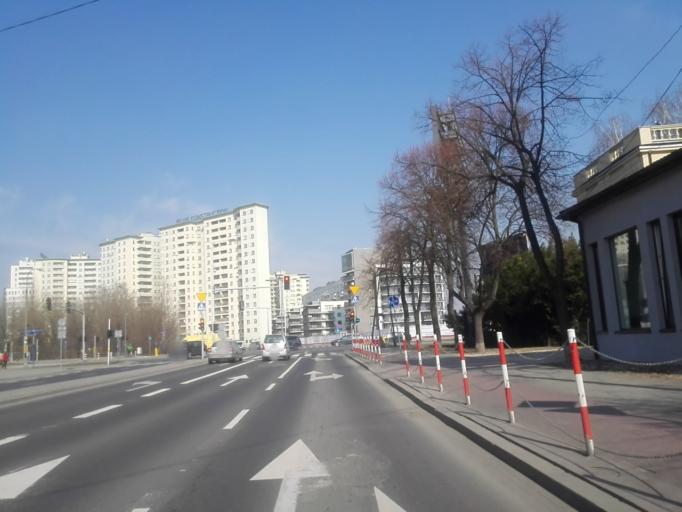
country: PL
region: Masovian Voivodeship
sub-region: Warszawa
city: Mokotow
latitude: 52.1777
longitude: 21.0276
